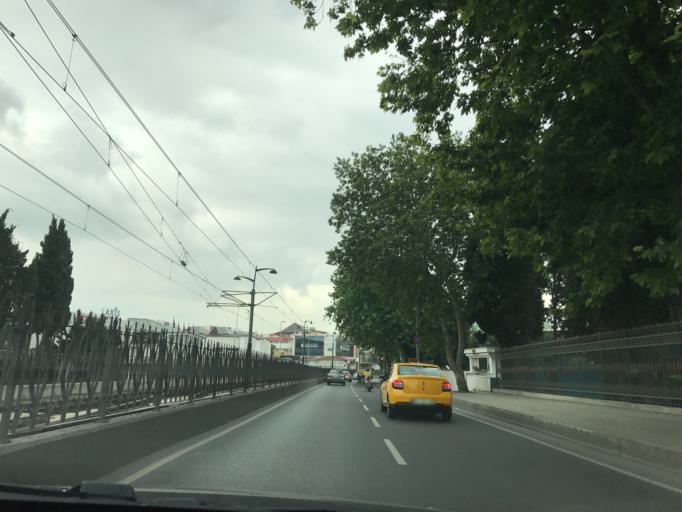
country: TR
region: Istanbul
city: Istanbul
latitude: 41.0348
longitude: 28.9264
